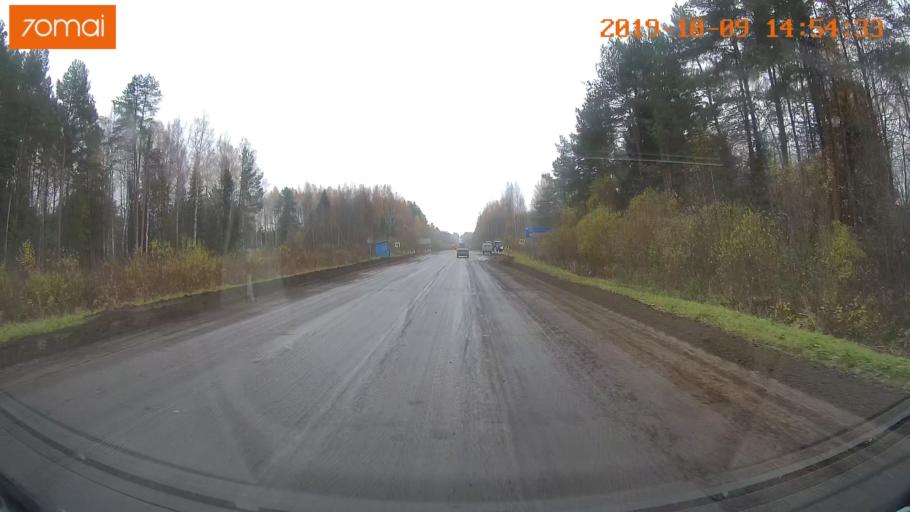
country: RU
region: Kostroma
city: Chistyye Bory
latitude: 58.3558
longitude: 41.6432
